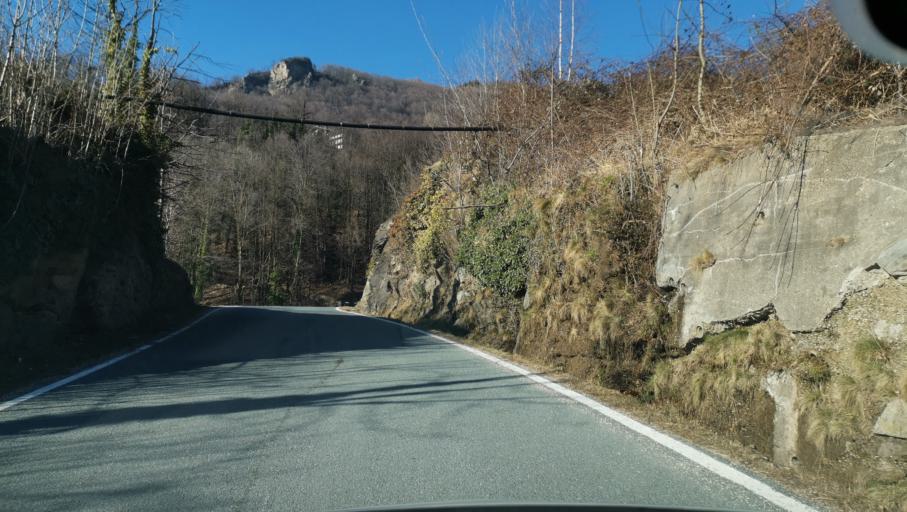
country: IT
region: Piedmont
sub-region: Provincia di Torino
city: Rora
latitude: 44.7886
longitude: 7.2007
